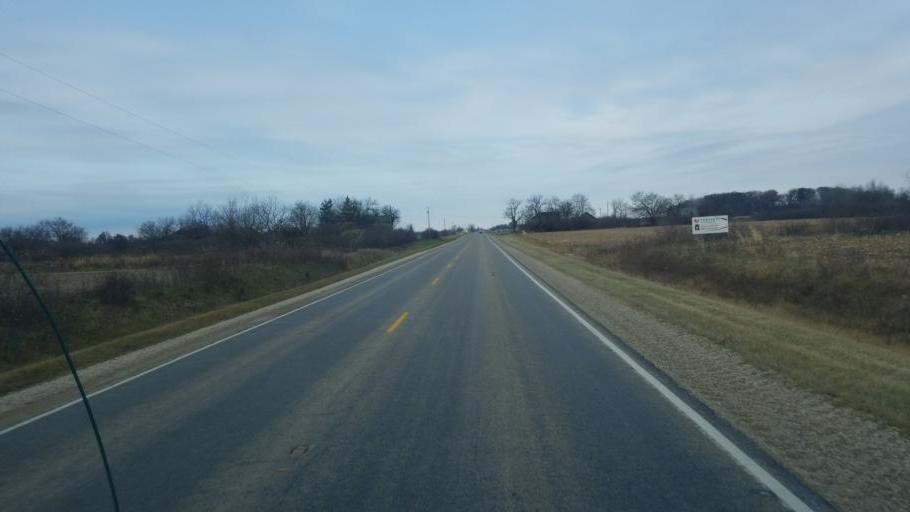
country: US
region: Indiana
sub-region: Adams County
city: Geneva
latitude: 40.5423
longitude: -84.8809
